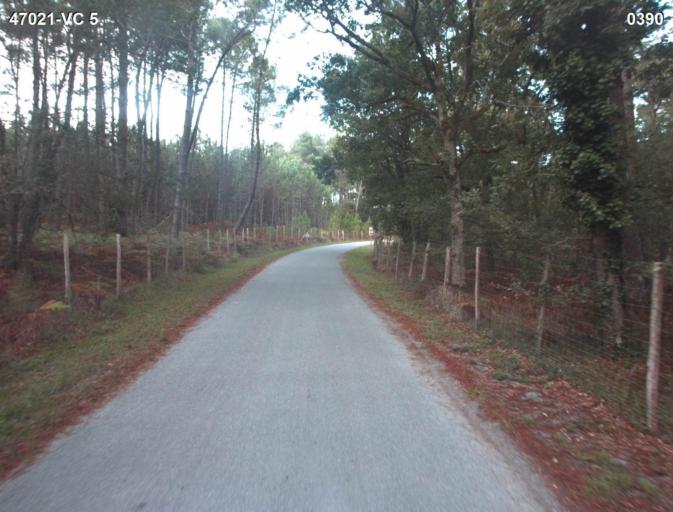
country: FR
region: Aquitaine
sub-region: Departement du Lot-et-Garonne
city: Barbaste
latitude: 44.1399
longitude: 0.2898
